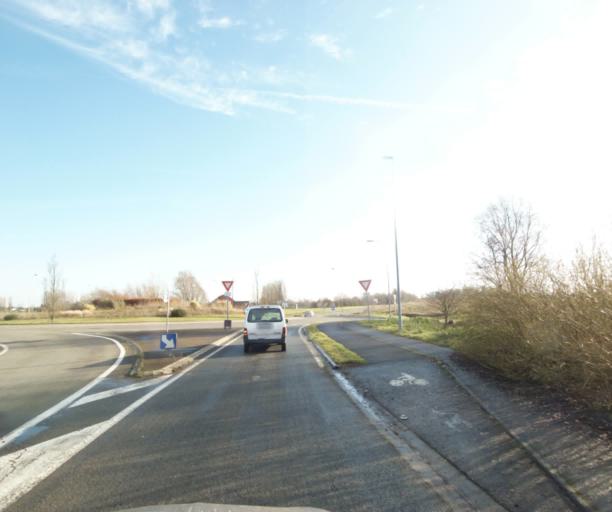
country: FR
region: Nord-Pas-de-Calais
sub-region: Departement du Nord
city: Saultain
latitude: 50.3343
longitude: 3.5889
